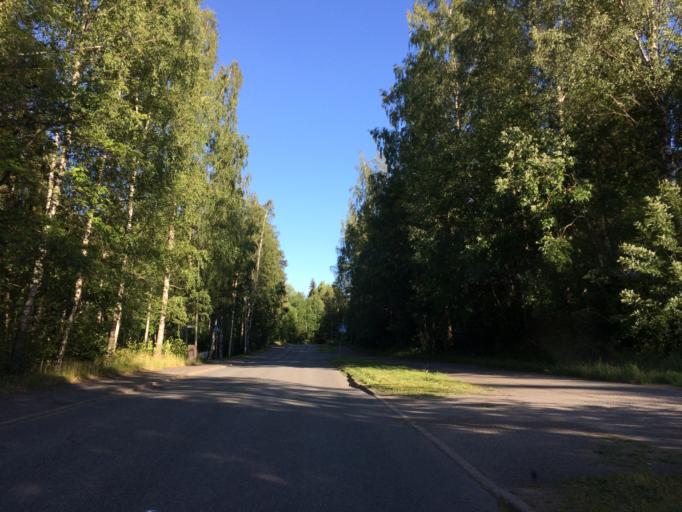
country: FI
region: Haeme
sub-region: Haemeenlinna
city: Haemeenlinna
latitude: 60.9832
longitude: 24.5189
